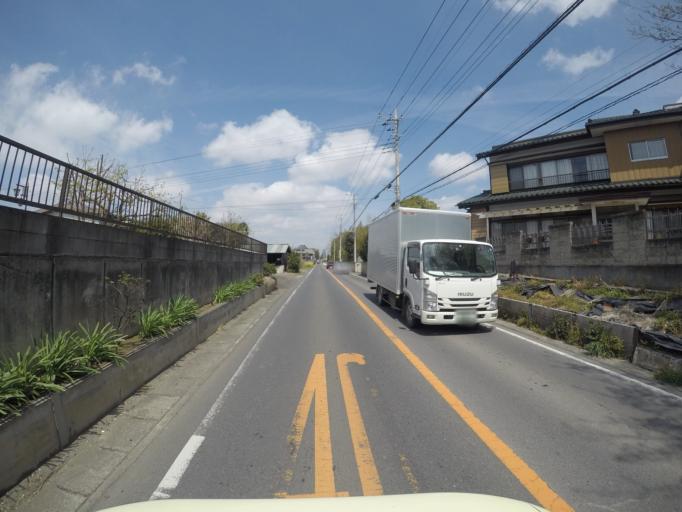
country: JP
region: Ibaraki
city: Shimodate
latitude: 36.2660
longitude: 140.0200
